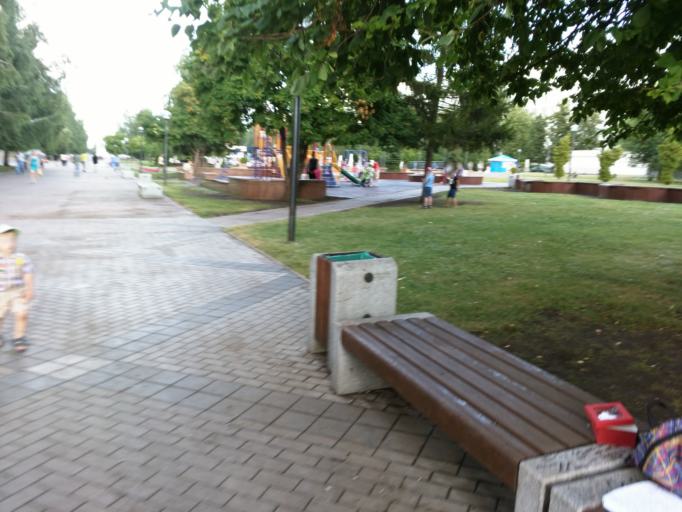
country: RU
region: Tatarstan
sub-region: Tukayevskiy Rayon
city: Naberezhnyye Chelny
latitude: 55.7422
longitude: 52.4159
